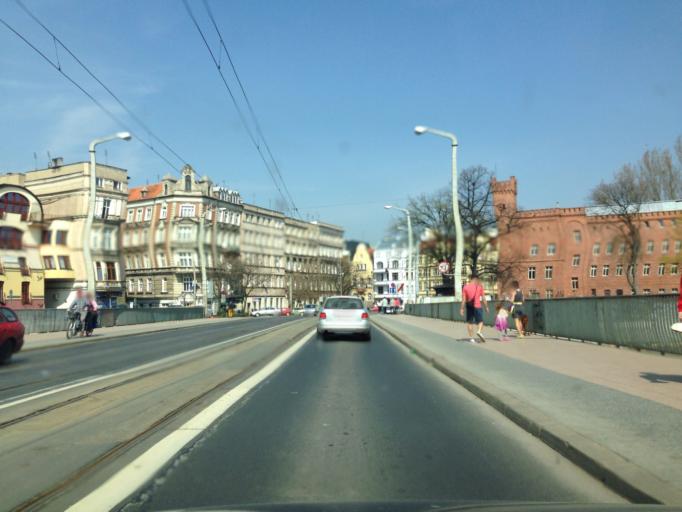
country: PL
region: Lower Silesian Voivodeship
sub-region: Powiat wroclawski
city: Wroclaw
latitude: 51.1154
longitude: 17.0338
